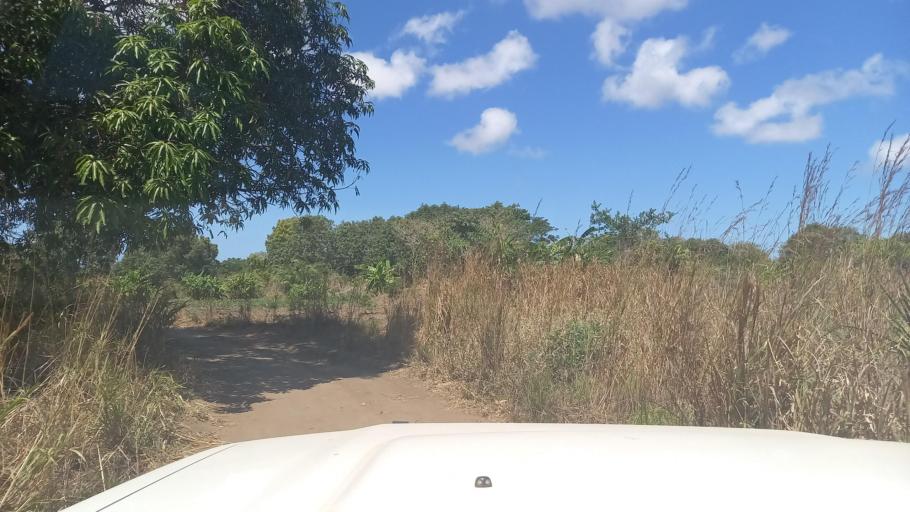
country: MZ
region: Cabo Delgado
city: Pemba
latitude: -13.4241
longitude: 40.4822
